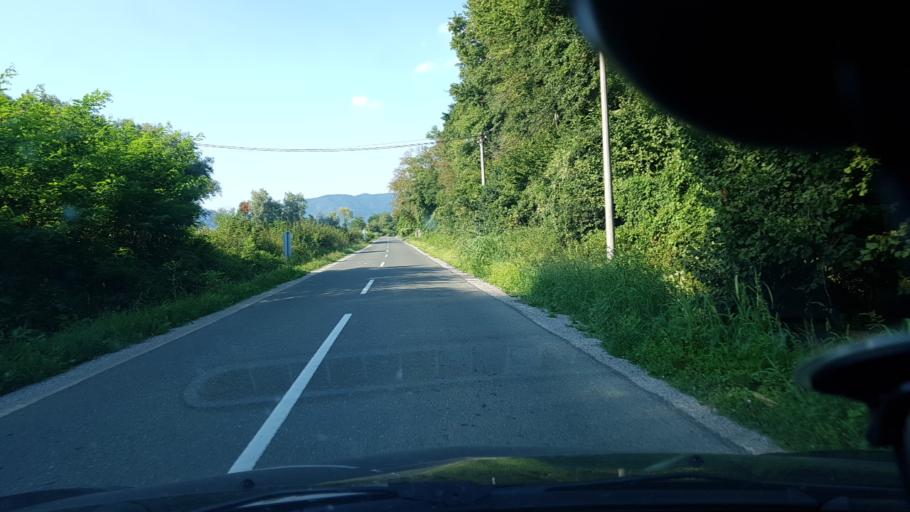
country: SI
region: Bistrica ob Sotli
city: Bistrica ob Sotli
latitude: 46.0056
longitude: 15.7132
